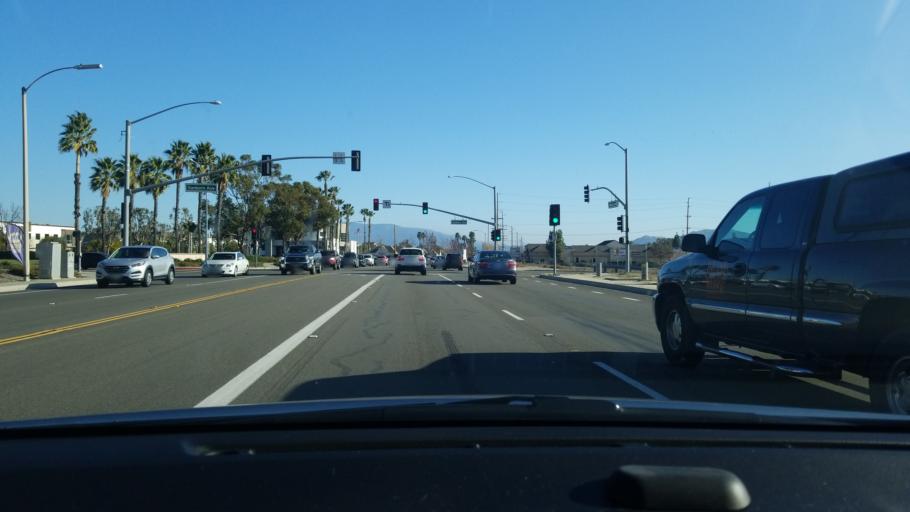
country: US
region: California
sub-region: Riverside County
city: Temecula
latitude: 33.5245
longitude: -117.1688
